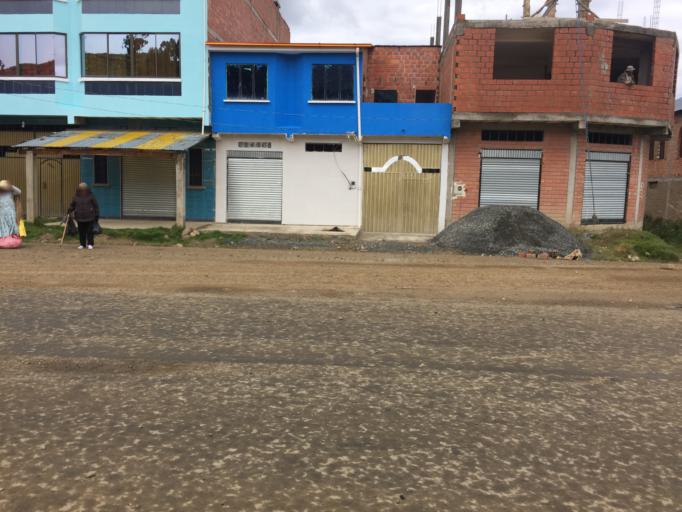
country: BO
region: La Paz
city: San Pablo
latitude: -16.1752
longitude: -68.7881
